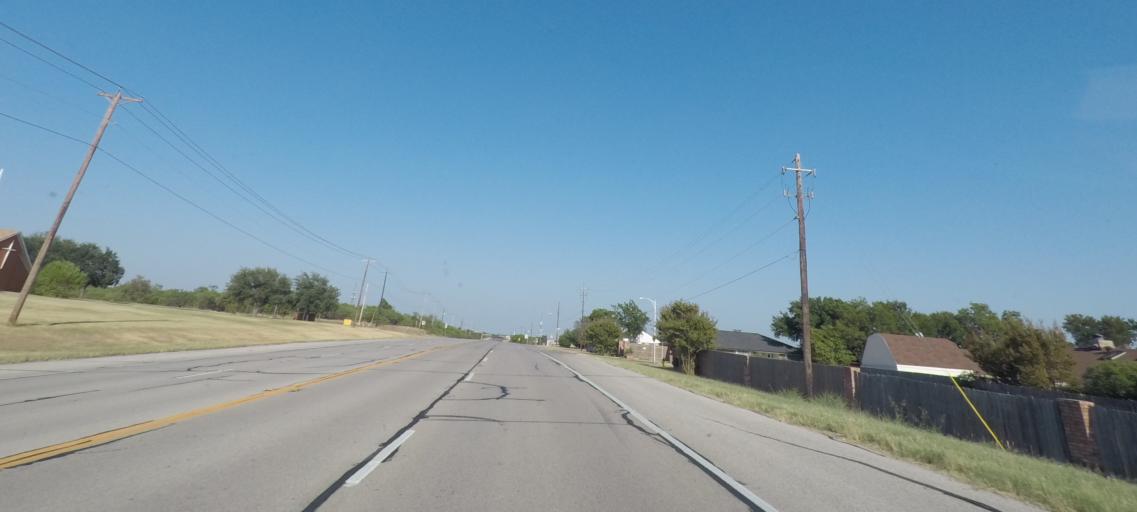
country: US
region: Texas
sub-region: Archer County
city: Holliday
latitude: 33.8594
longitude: -98.5979
